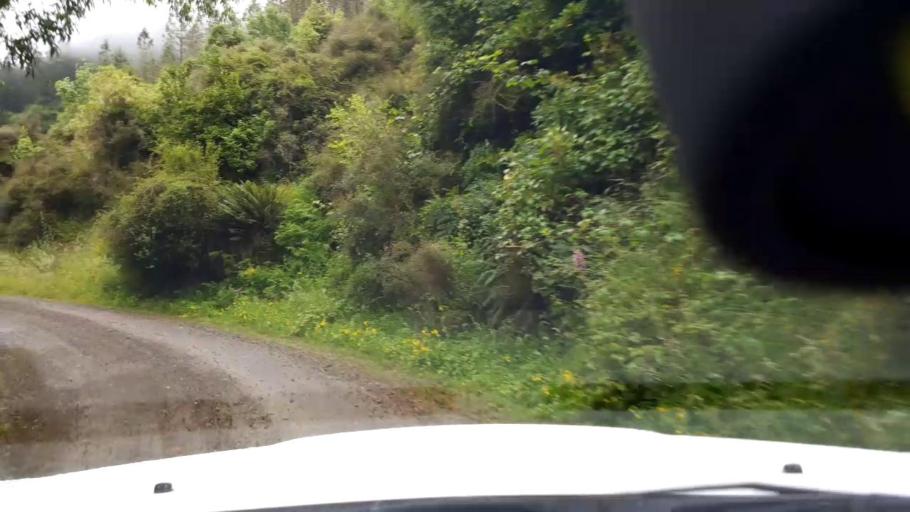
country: NZ
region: Canterbury
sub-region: Timaru District
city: Pleasant Point
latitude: -44.0422
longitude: 171.0186
